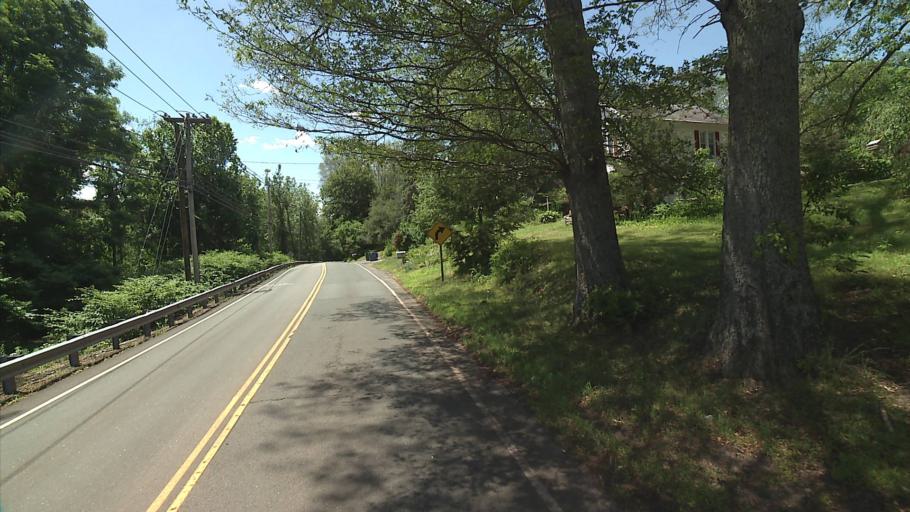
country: US
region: Connecticut
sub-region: Middlesex County
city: East Hampton
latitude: 41.5704
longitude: -72.5047
